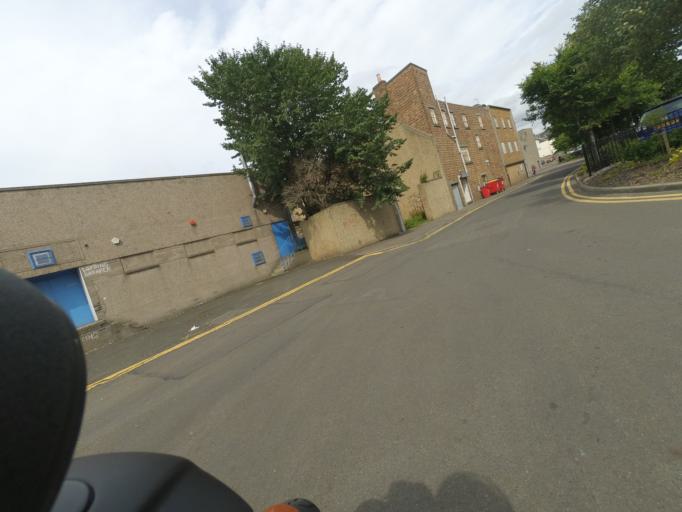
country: GB
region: Scotland
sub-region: Fife
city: Leven
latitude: 56.1936
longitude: -2.9975
